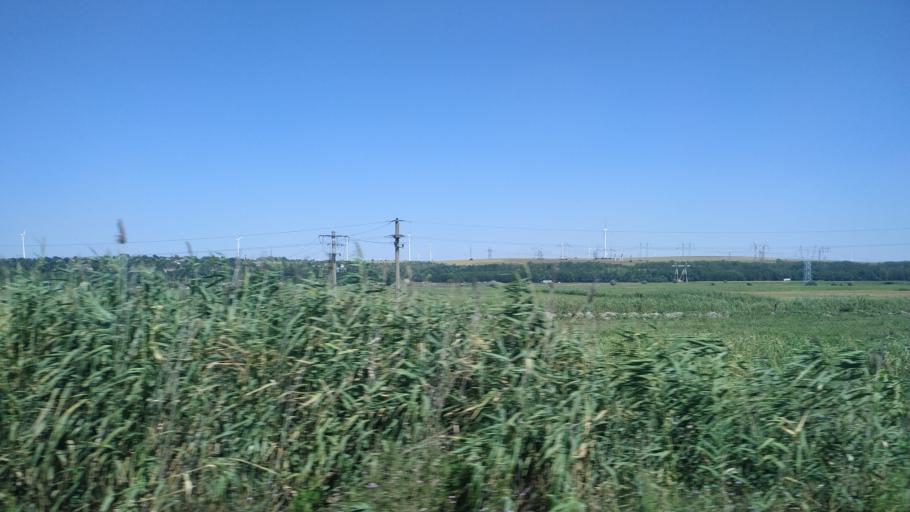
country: RO
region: Constanta
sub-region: Comuna Saligny
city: Faclia
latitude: 44.2708
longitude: 28.1149
